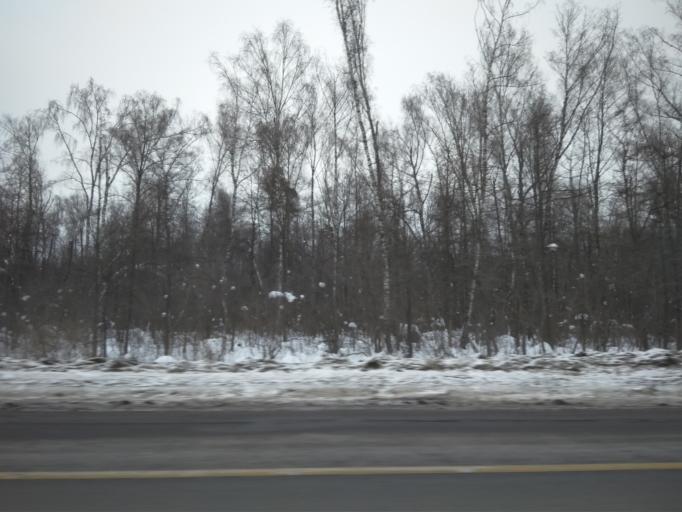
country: RU
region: Moskovskaya
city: Petrovskaya
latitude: 55.5471
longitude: 37.7949
